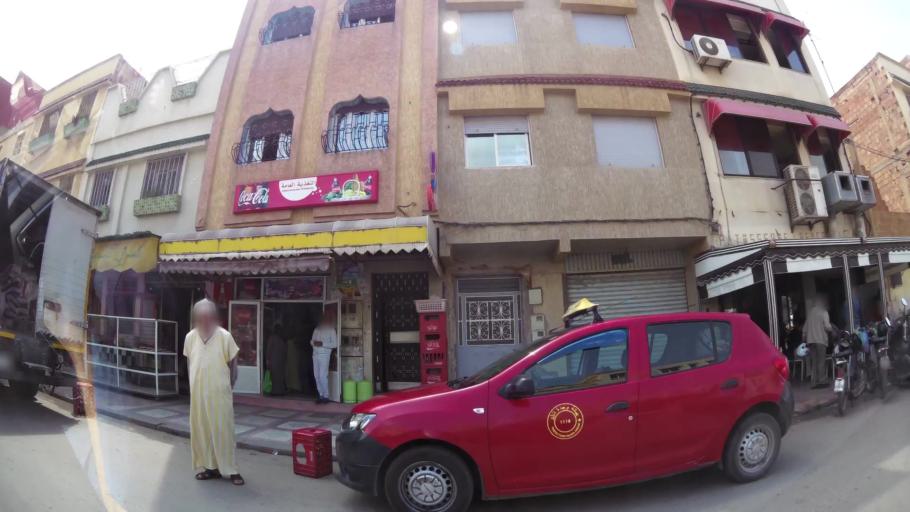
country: MA
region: Oriental
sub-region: Oujda-Angad
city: Oujda
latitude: 34.6830
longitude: -1.8828
